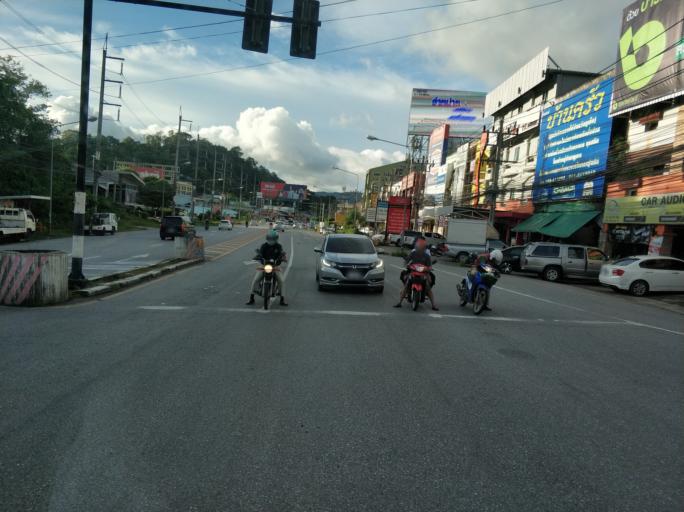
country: TH
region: Phuket
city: Wichit
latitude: 7.8938
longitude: 98.3655
